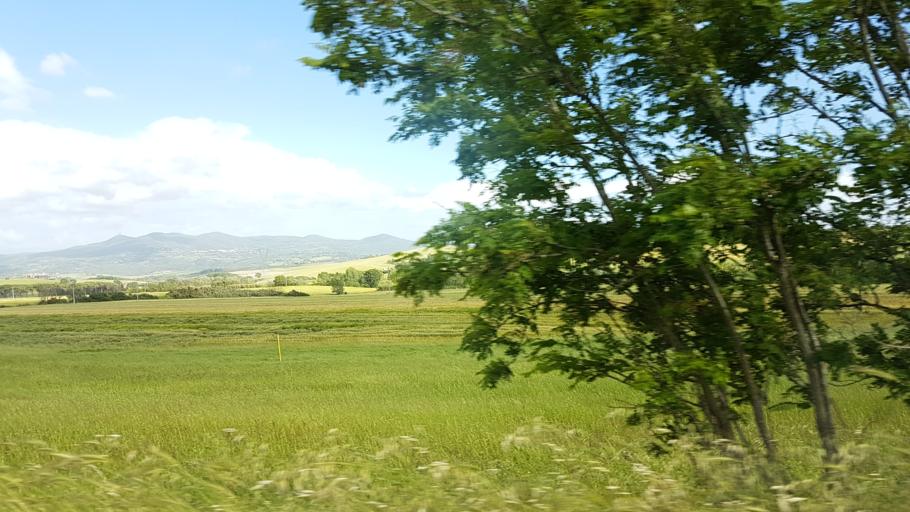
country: IT
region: Tuscany
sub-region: Provincia di Livorno
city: Rosignano Marittimo
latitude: 43.4392
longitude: 10.4935
